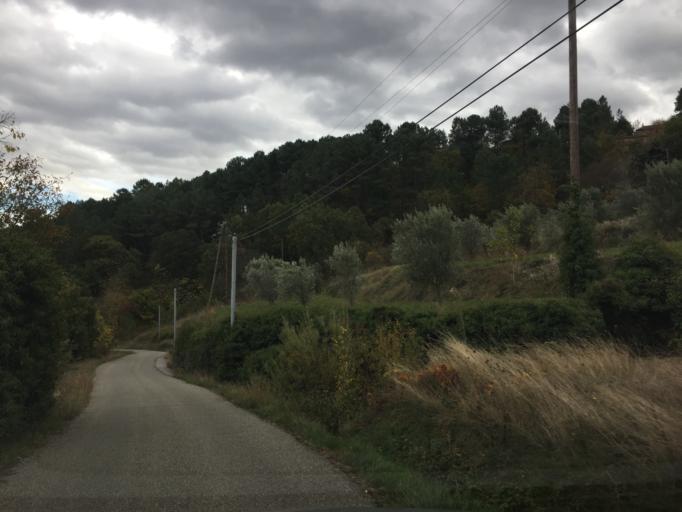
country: FR
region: Rhone-Alpes
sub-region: Departement de l'Ardeche
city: Les Vans
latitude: 44.4252
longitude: 4.0809
